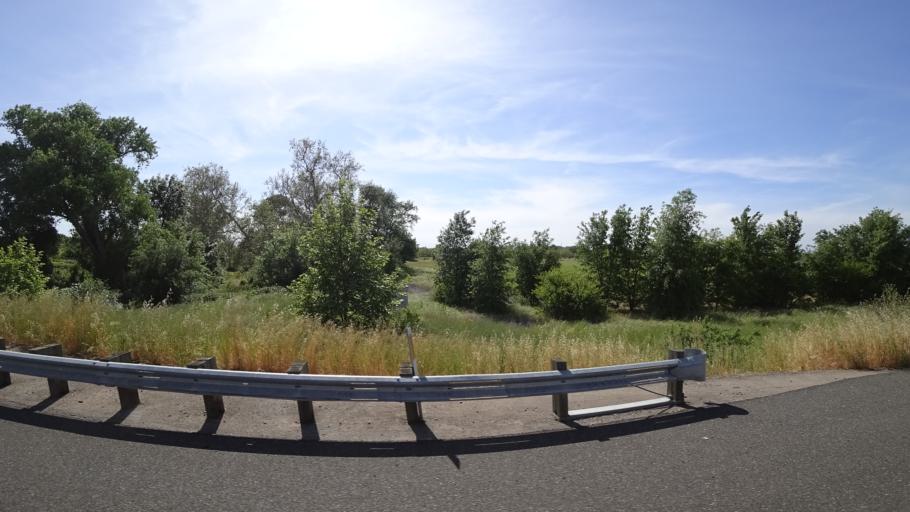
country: US
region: California
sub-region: Tehama County
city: Gerber
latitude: 40.0907
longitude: -122.1006
